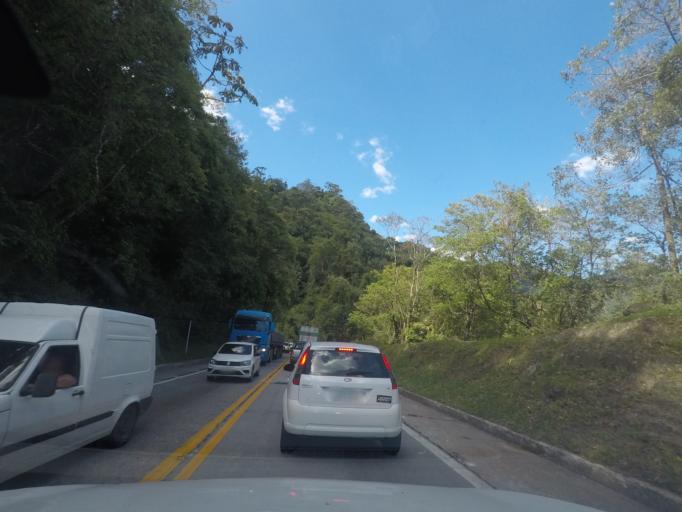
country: BR
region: Rio de Janeiro
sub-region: Guapimirim
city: Guapimirim
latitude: -22.4817
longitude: -42.9984
